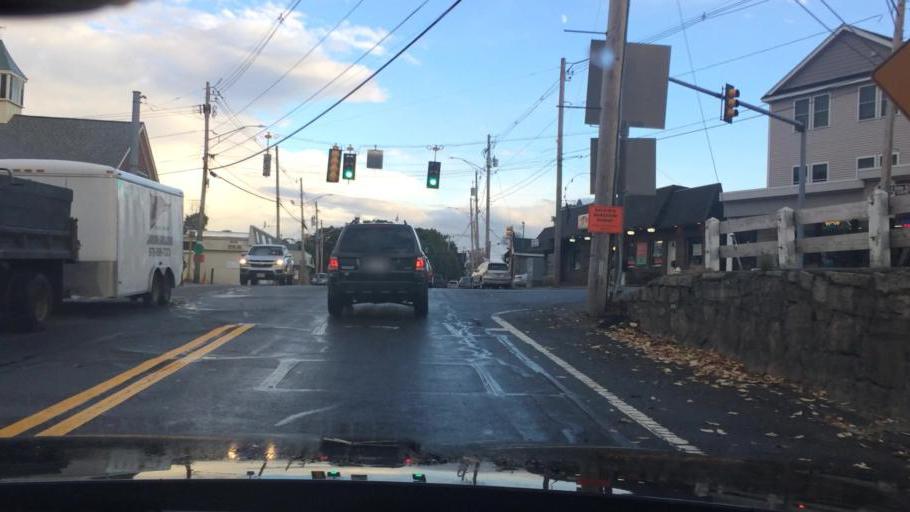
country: US
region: Massachusetts
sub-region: Middlesex County
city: Chelmsford
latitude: 42.6398
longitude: -71.3840
